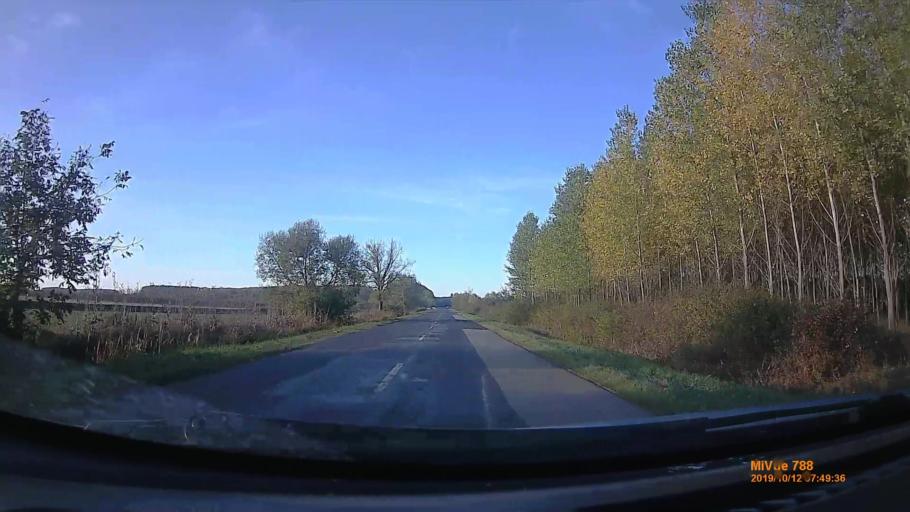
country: HU
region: Hajdu-Bihar
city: Biharkeresztes
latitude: 47.1612
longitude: 21.7440
